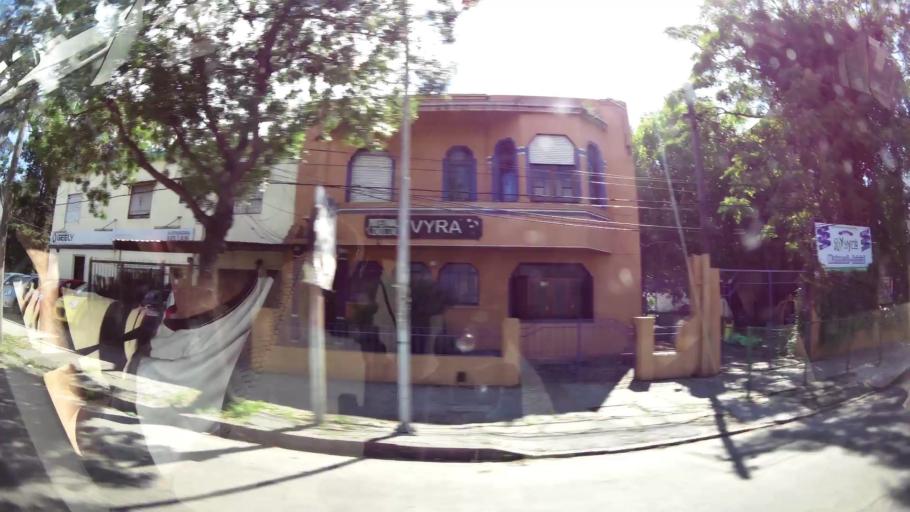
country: UY
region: Montevideo
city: Montevideo
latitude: -34.8503
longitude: -56.1981
